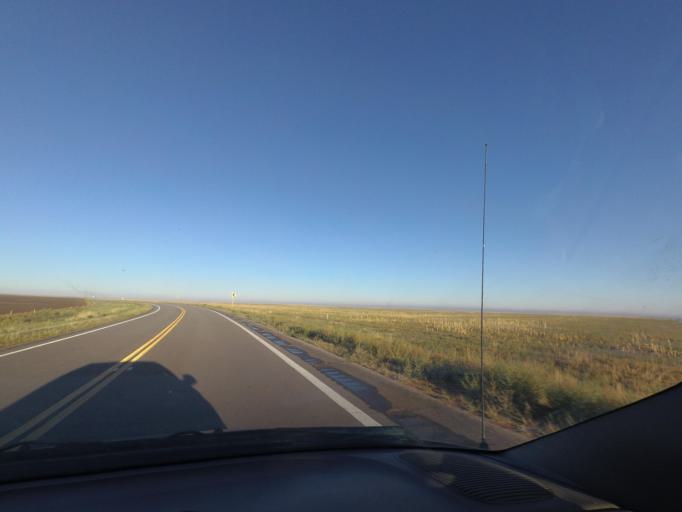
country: US
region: Colorado
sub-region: Washington County
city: Akron
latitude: 39.7271
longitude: -103.1040
